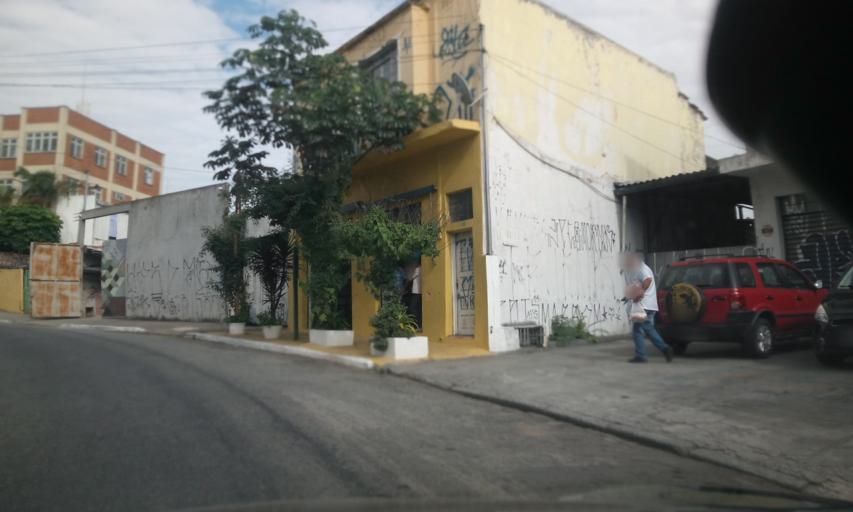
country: BR
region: Sao Paulo
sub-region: Sao Caetano Do Sul
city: Sao Caetano do Sul
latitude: -23.6155
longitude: -46.6064
